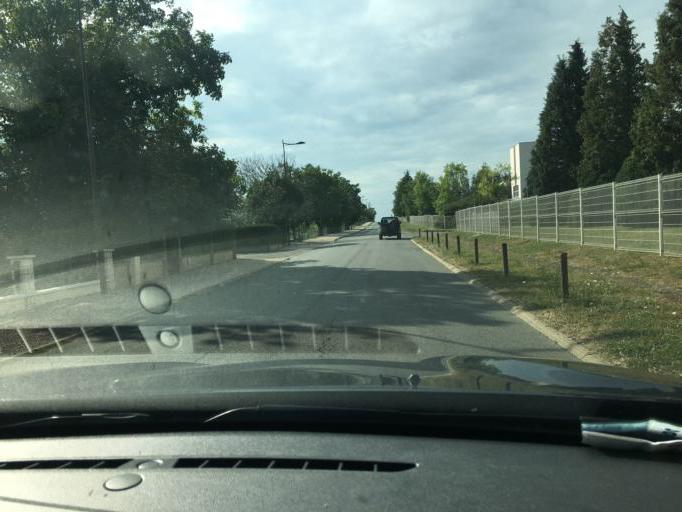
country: FR
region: Centre
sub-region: Departement du Cher
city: Rians
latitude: 47.1895
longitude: 2.6077
